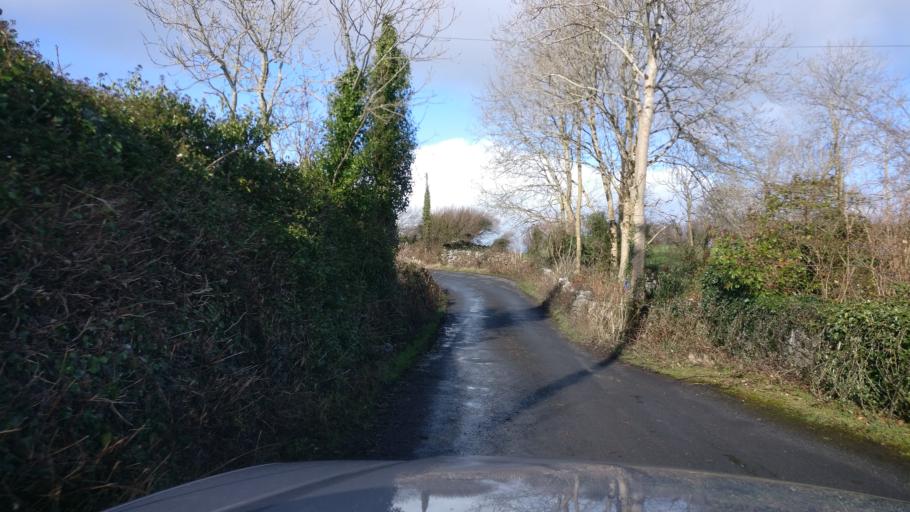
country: IE
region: Connaught
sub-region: County Galway
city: Athenry
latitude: 53.2302
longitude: -8.7584
